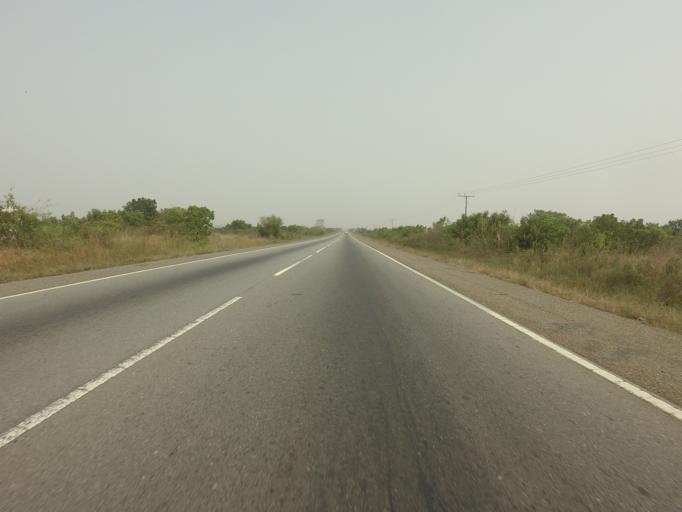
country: GH
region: Greater Accra
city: Tema
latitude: 5.8788
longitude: 0.3918
